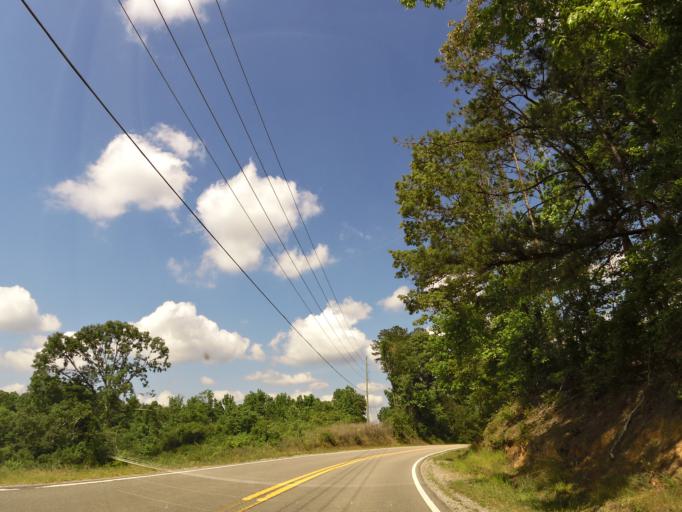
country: US
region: Alabama
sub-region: Marion County
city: Guin
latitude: 33.9960
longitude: -87.8636
